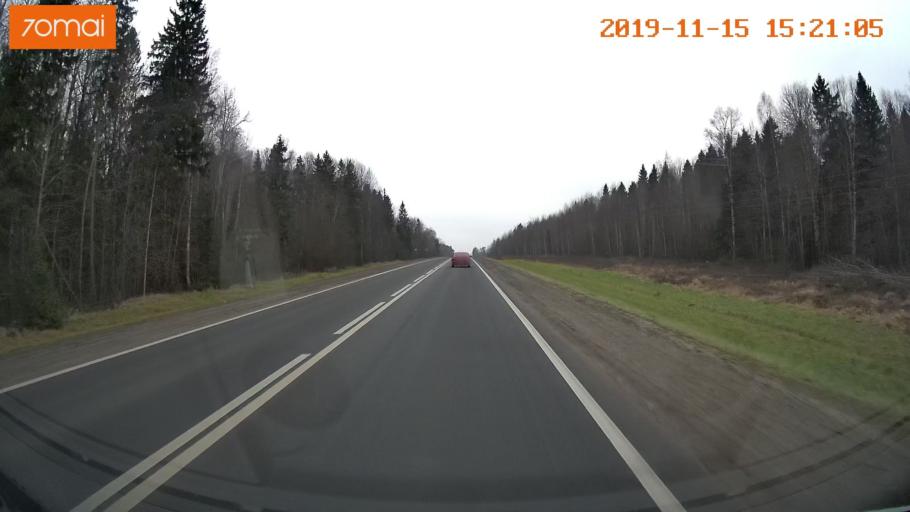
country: RU
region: Jaroslavl
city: Danilov
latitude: 58.2164
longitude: 40.1512
